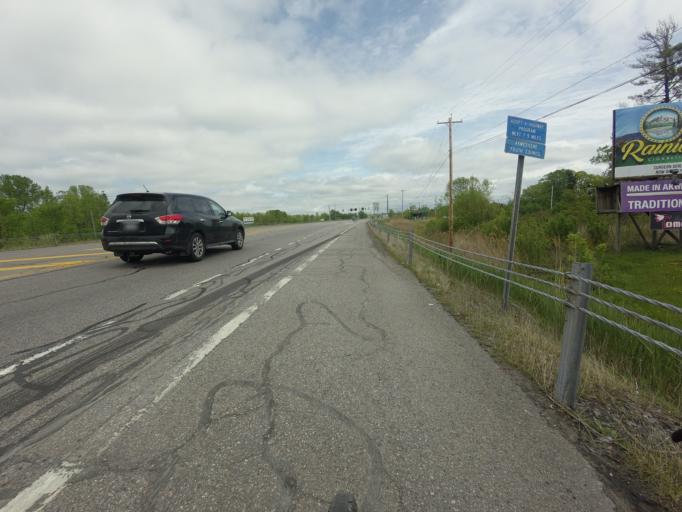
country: CA
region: Ontario
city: Cornwall
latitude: 44.9795
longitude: -74.7215
